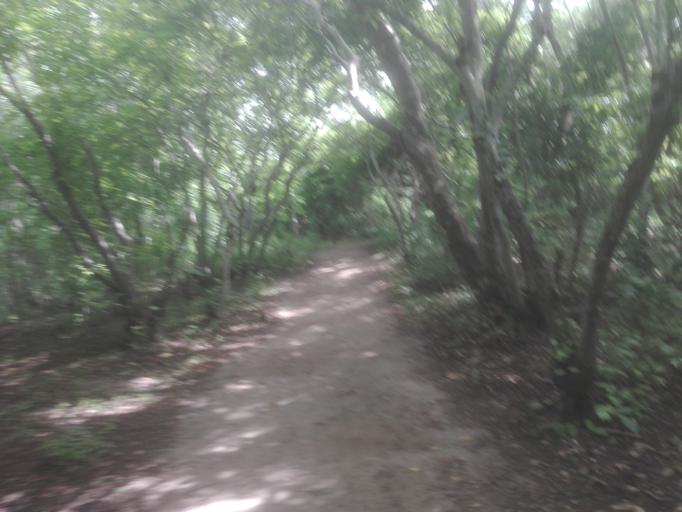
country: CO
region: Bolivar
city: Turbana
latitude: 10.1797
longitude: -75.7340
